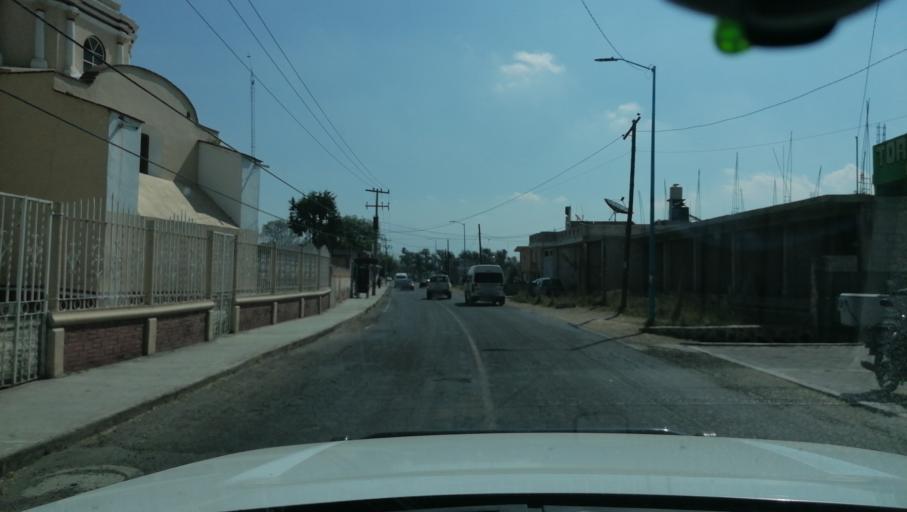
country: MX
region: Tlaxcala
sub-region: Tetlatlahuca
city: Tetlatlahuca
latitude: 19.2313
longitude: -98.2950
